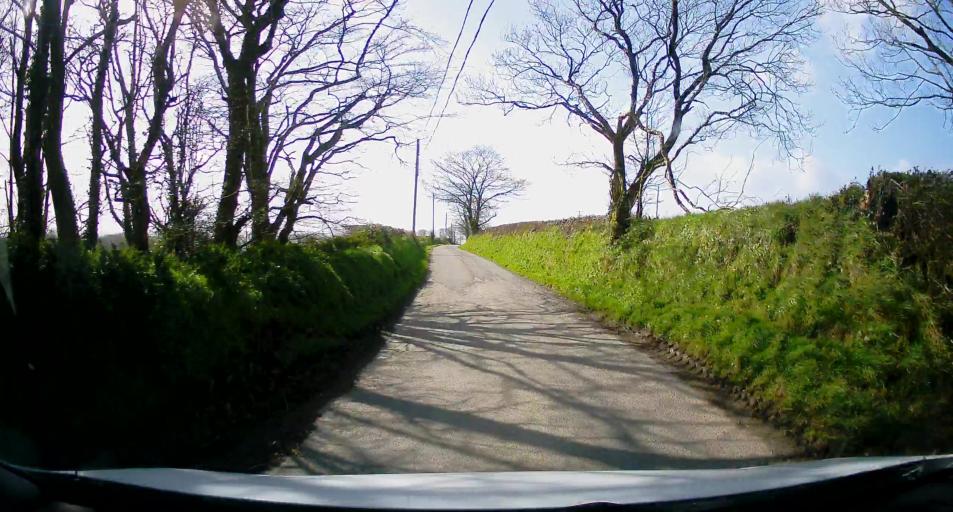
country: GB
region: Wales
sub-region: County of Ceredigion
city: Aberporth
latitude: 52.0740
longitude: -4.5499
